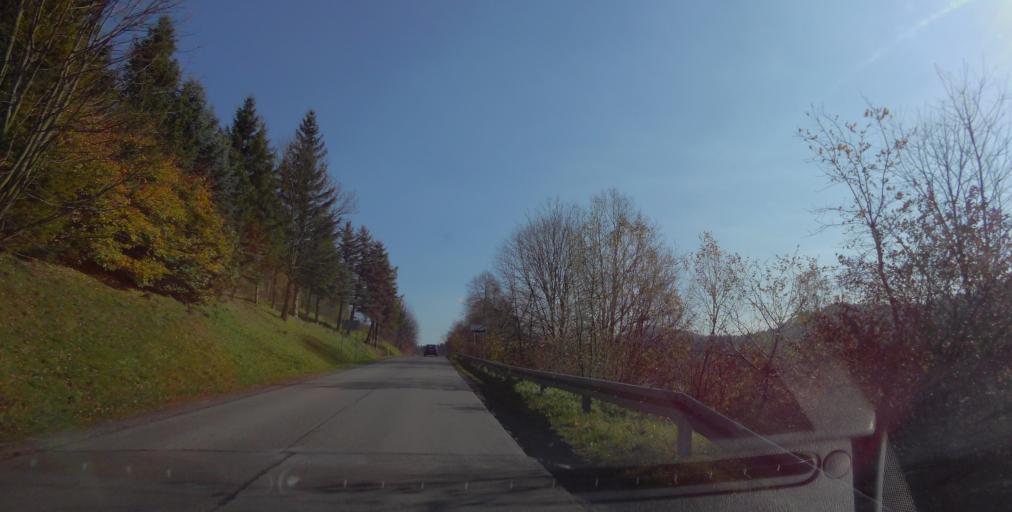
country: PL
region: Subcarpathian Voivodeship
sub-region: Powiat leski
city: Polanczyk
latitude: 49.3336
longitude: 22.4191
